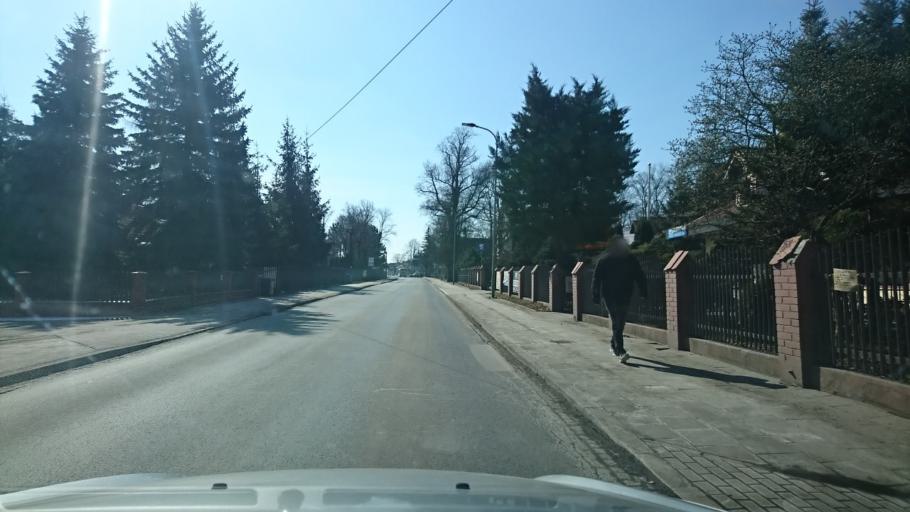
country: PL
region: Lesser Poland Voivodeship
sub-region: Powiat wielicki
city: Kokotow
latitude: 50.0677
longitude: 20.0524
